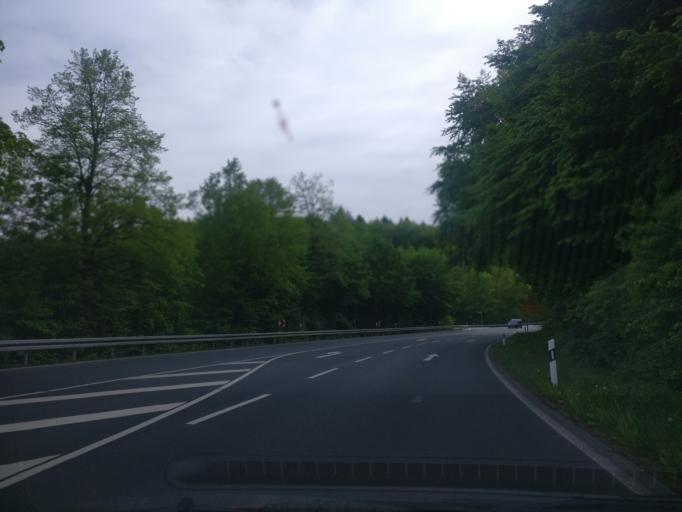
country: DE
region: Hesse
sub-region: Regierungsbezirk Kassel
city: Fuldatal
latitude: 51.3657
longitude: 9.5293
